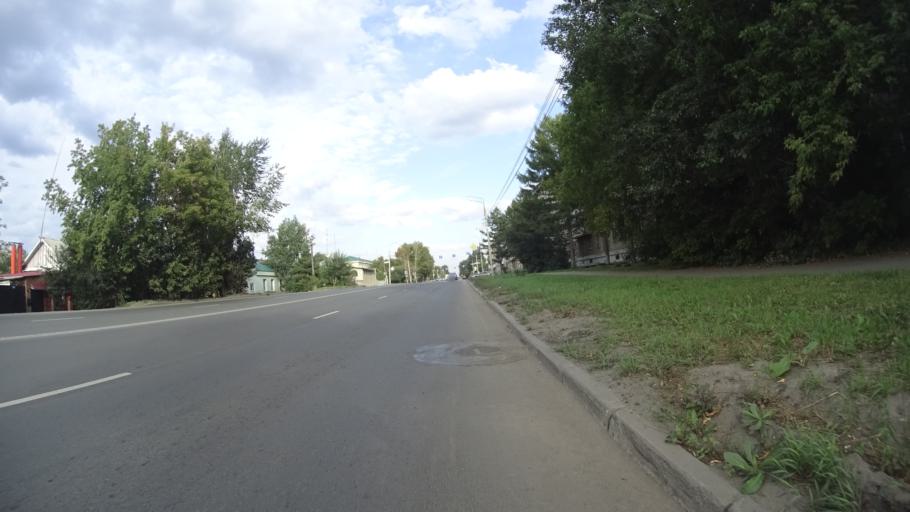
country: RU
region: Chelyabinsk
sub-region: Gorod Chelyabinsk
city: Chelyabinsk
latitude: 55.1985
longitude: 61.3513
